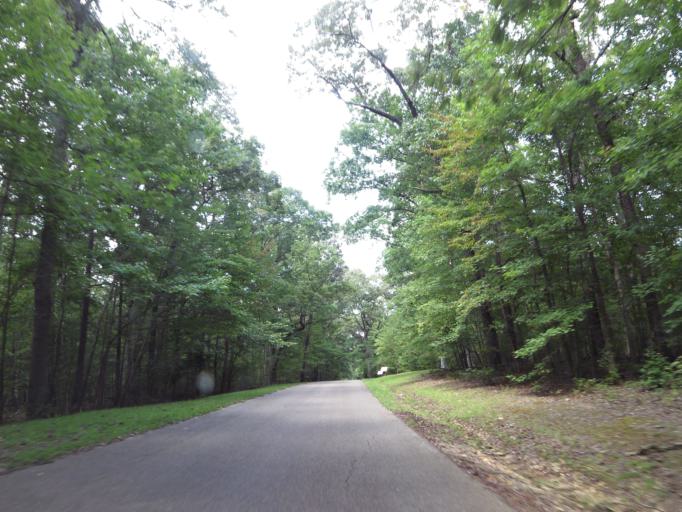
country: US
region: Tennessee
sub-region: Hardin County
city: Crump
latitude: 35.1335
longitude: -88.3397
